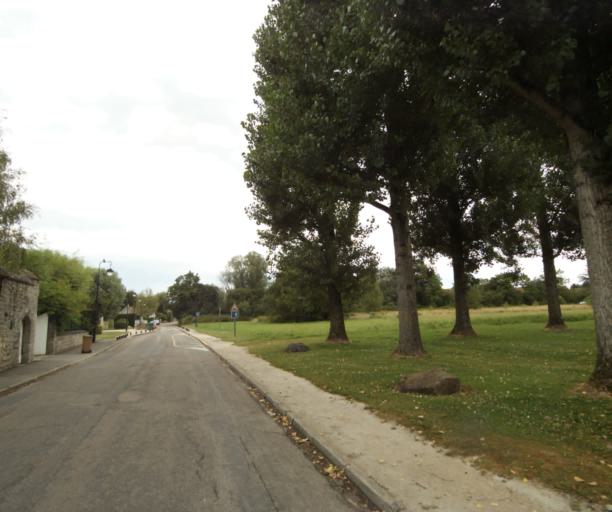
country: FR
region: Ile-de-France
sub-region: Departement de Seine-et-Marne
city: Arbonne-la-Foret
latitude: 48.4147
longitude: 2.5646
